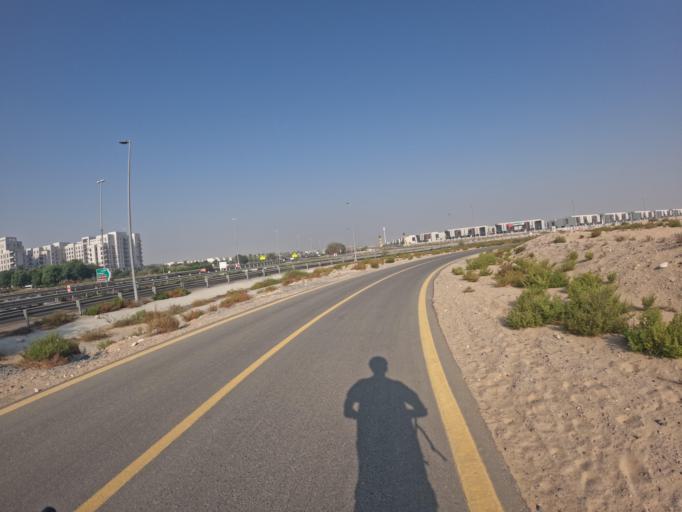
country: AE
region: Dubai
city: Dubai
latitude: 25.0120
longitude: 55.2921
